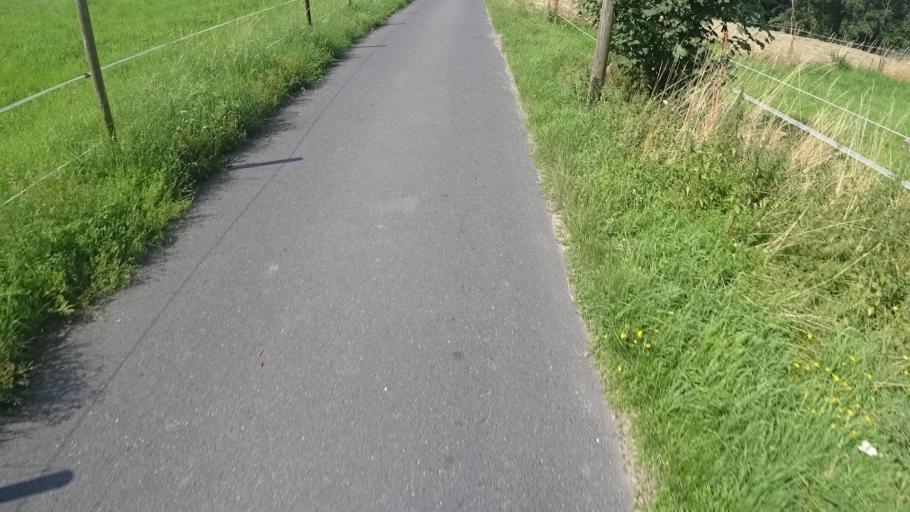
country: DE
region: Rheinland-Pfalz
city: Sankt Katharinen
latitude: 50.5776
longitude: 7.3479
